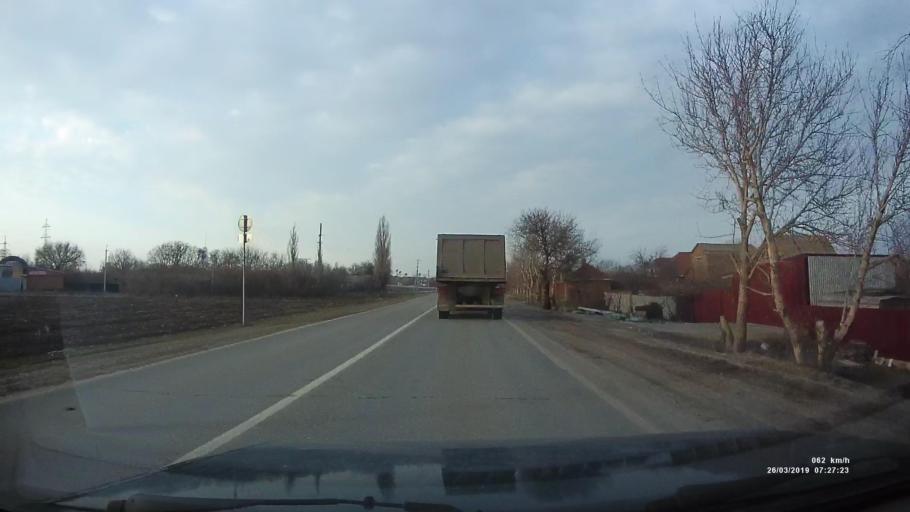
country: RU
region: Rostov
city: Taganrog
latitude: 47.2627
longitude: 38.8287
